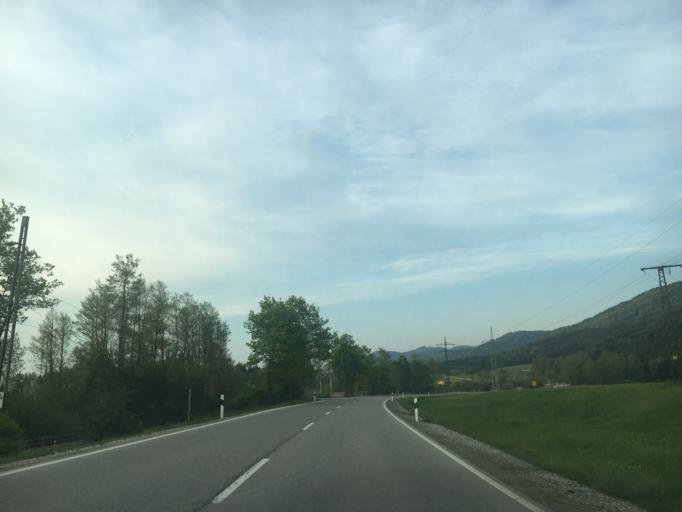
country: DE
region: Bavaria
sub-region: Upper Bavaria
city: Kochel
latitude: 47.6649
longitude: 11.3814
